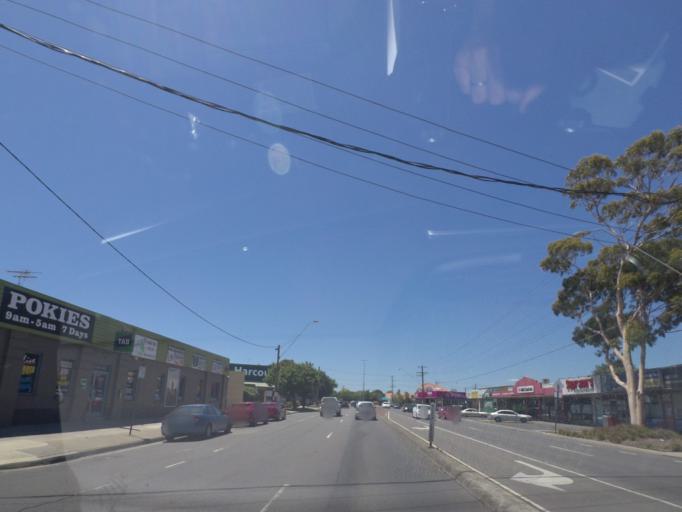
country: AU
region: Victoria
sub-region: Whittlesea
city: Epping
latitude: -37.6496
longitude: 145.0251
